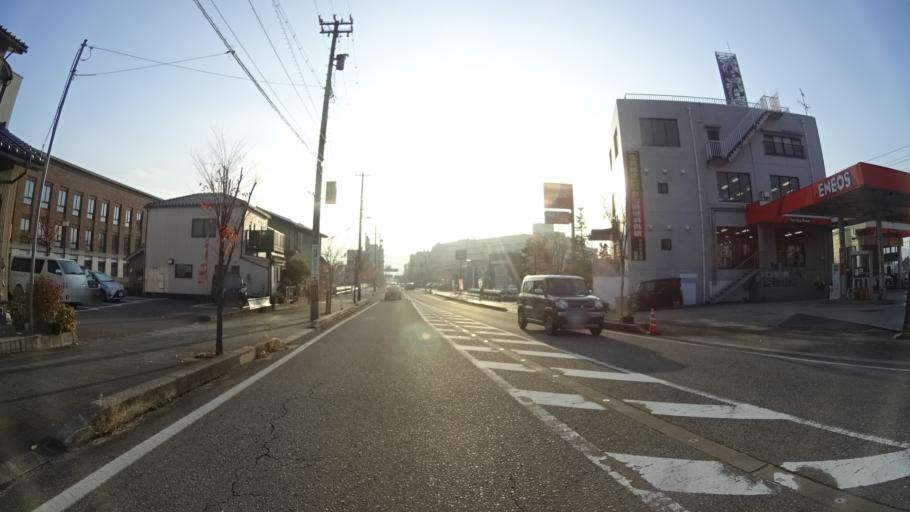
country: JP
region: Ishikawa
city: Nanao
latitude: 37.0450
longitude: 136.9609
